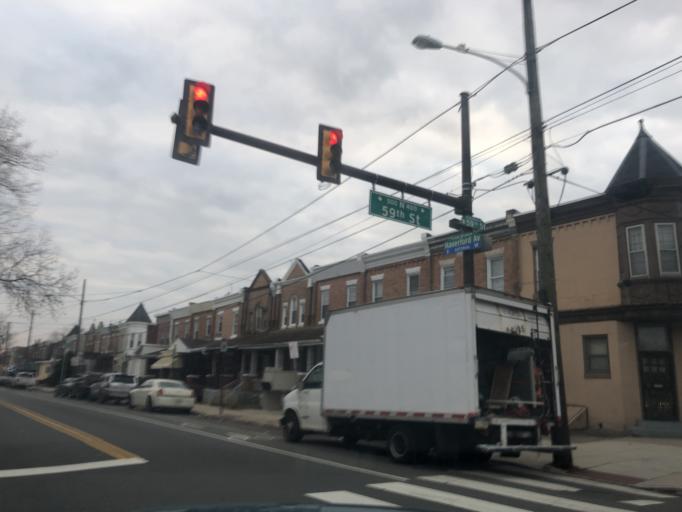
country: US
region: Pennsylvania
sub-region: Delaware County
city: Millbourne
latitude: 39.9690
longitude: -75.2373
